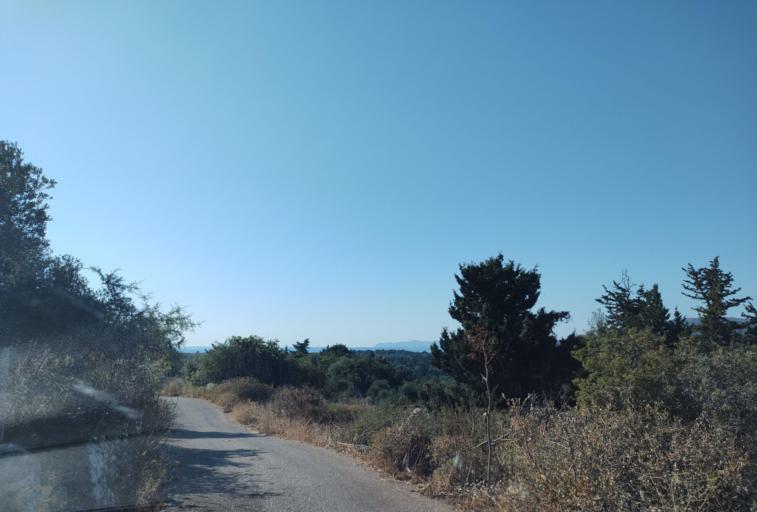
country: GR
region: Crete
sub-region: Nomos Chanias
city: Georgioupolis
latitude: 35.3961
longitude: 24.2368
